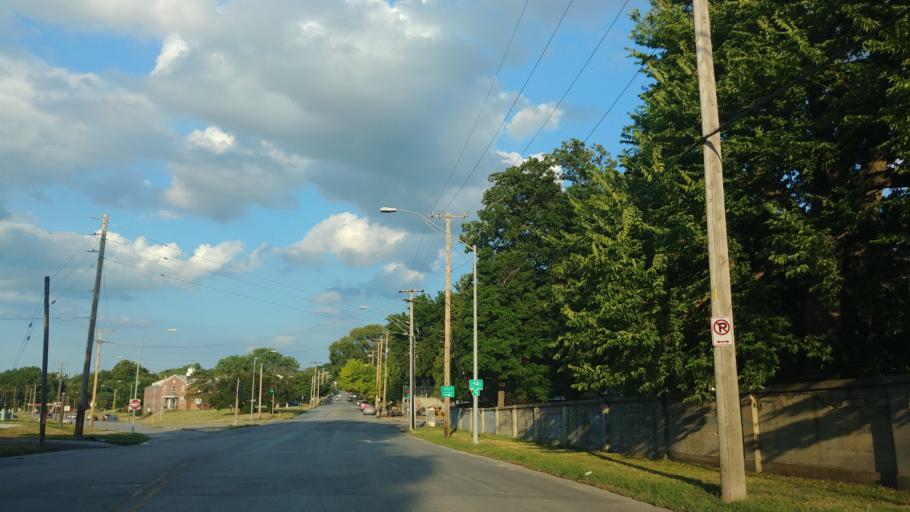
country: US
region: Missouri
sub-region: Clay County
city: North Kansas City
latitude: 39.0978
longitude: -94.5245
